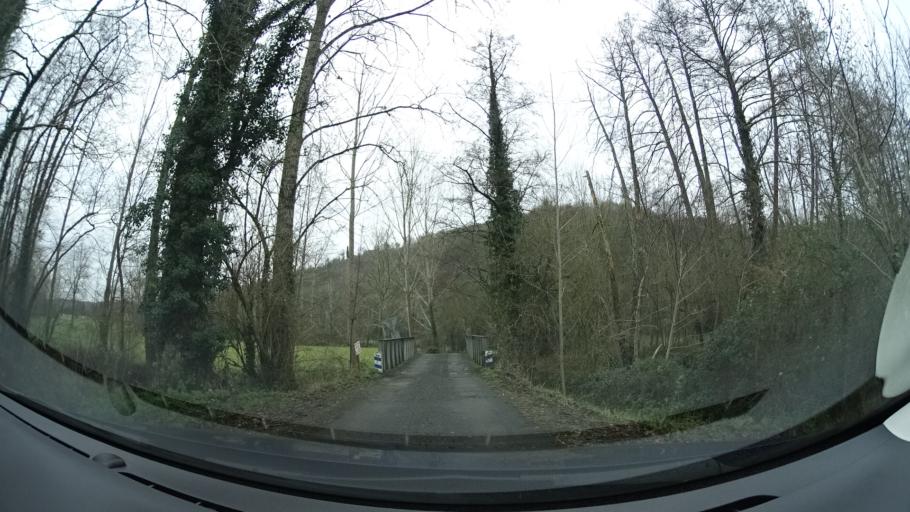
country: FR
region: Aquitaine
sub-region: Departement de la Dordogne
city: Belves
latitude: 44.8146
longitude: 0.9991
